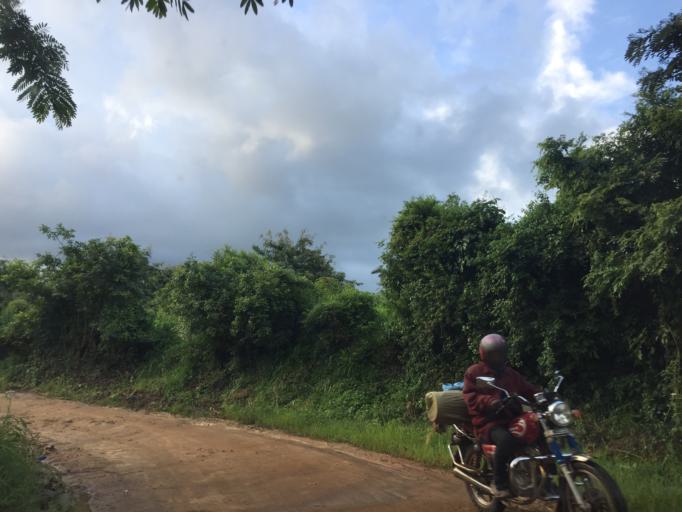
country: TZ
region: Tanga
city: Muheza
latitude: -5.1587
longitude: 38.7696
